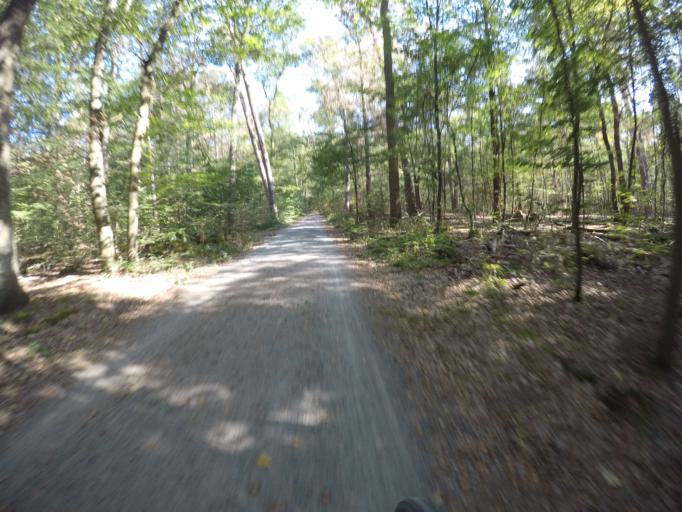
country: DE
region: Hesse
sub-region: Regierungsbezirk Darmstadt
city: Neu Isenburg
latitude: 50.0566
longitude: 8.6575
